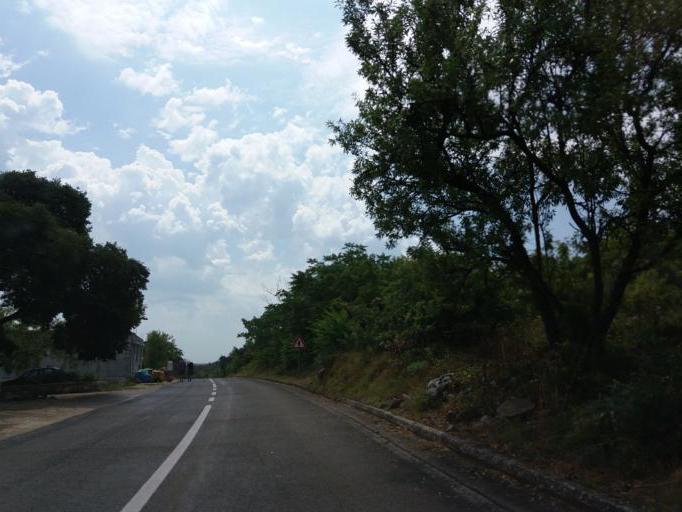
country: HR
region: Zadarska
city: Sali
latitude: 43.9351
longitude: 15.1566
